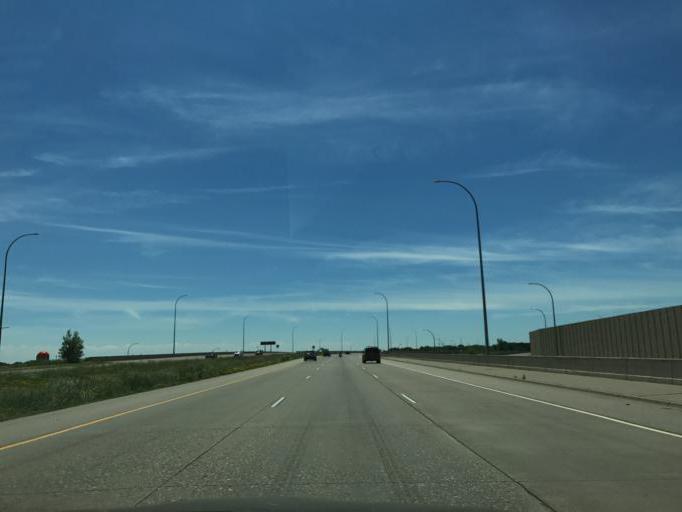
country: US
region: Minnesota
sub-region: Hennepin County
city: Osseo
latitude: 45.1119
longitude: -93.3918
